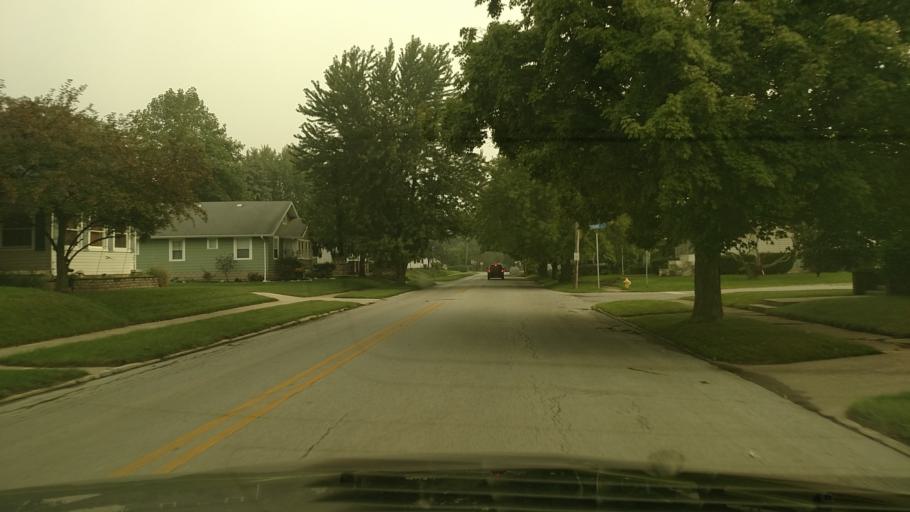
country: US
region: Indiana
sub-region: Howard County
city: Kokomo
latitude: 40.4677
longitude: -86.1364
